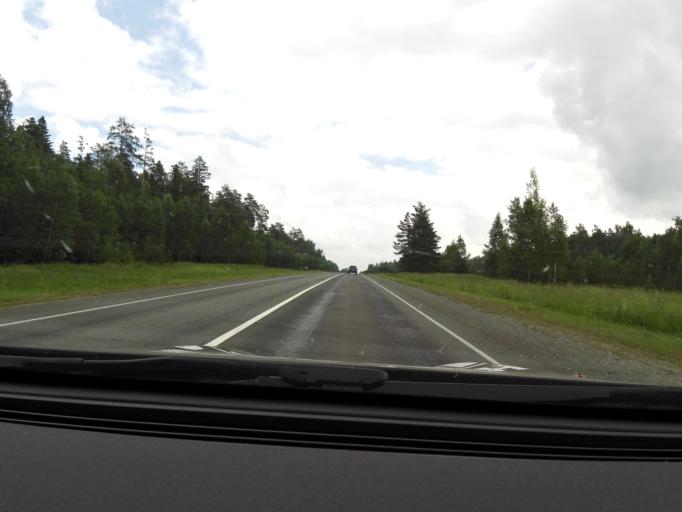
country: RU
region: Perm
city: Suksun
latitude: 56.9235
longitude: 57.5640
